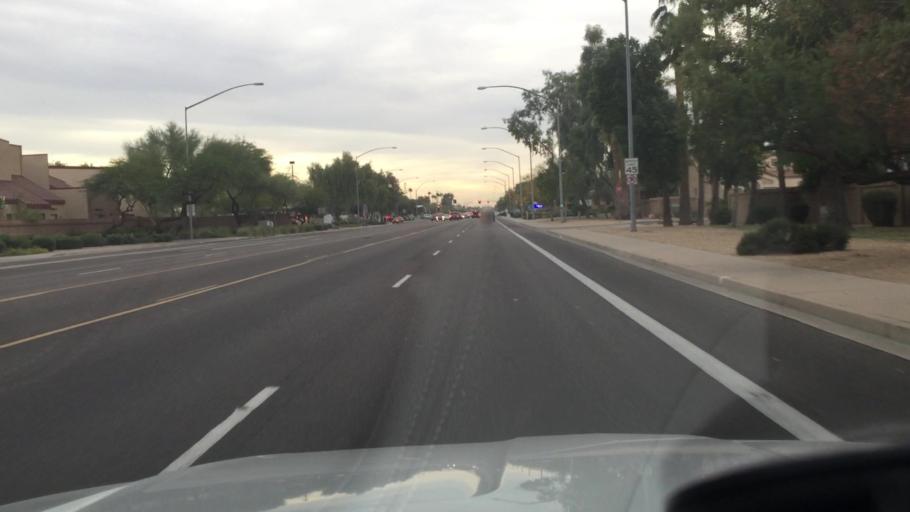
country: US
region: Arizona
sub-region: Maricopa County
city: Gilbert
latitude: 33.3969
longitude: -111.7539
